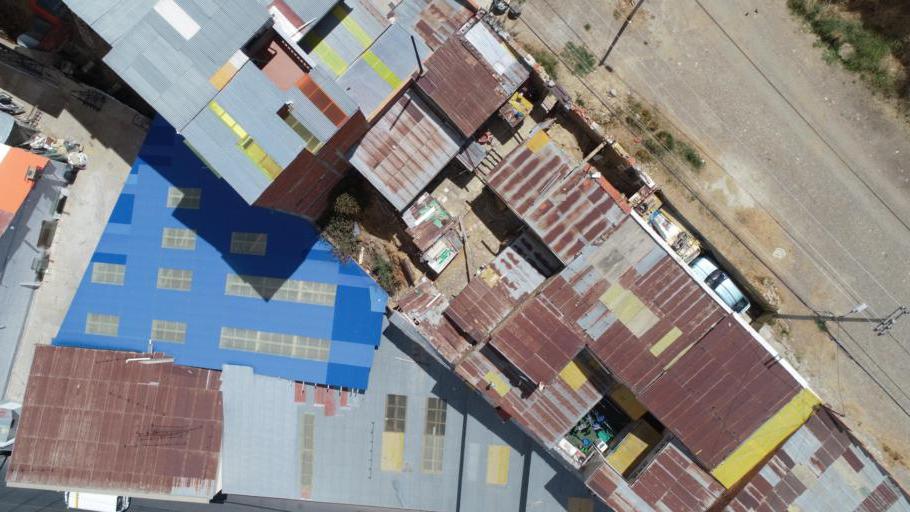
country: BO
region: La Paz
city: La Paz
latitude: -16.4809
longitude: -68.1508
